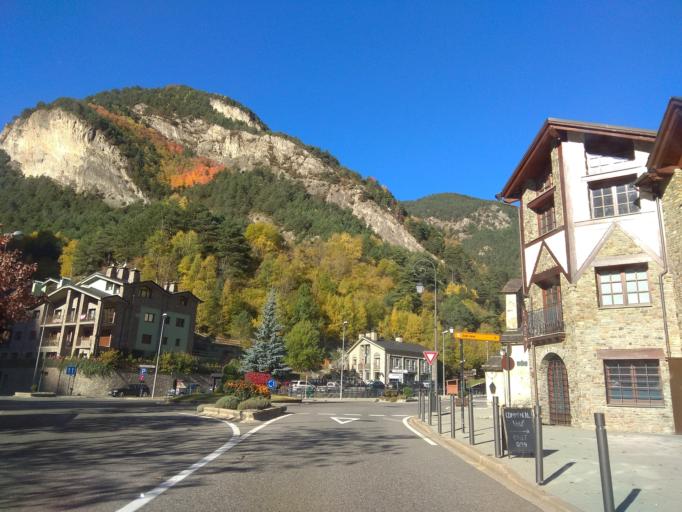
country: AD
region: La Massana
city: Arinsal
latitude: 42.5615
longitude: 1.4971
